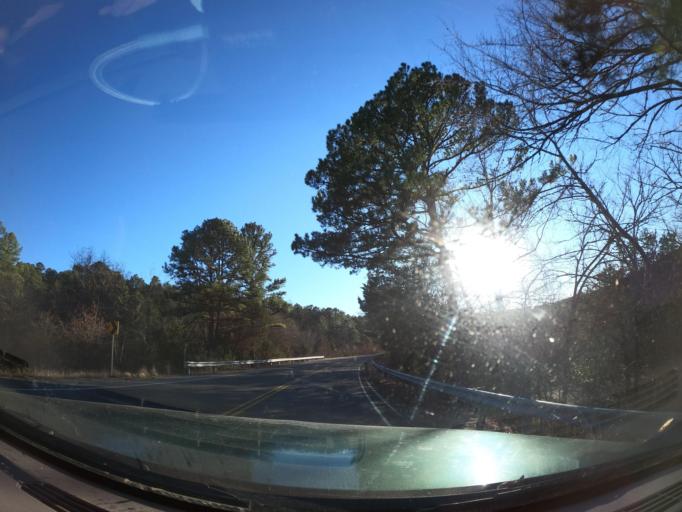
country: US
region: Oklahoma
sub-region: Latimer County
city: Wilburton
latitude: 34.9707
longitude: -95.3555
